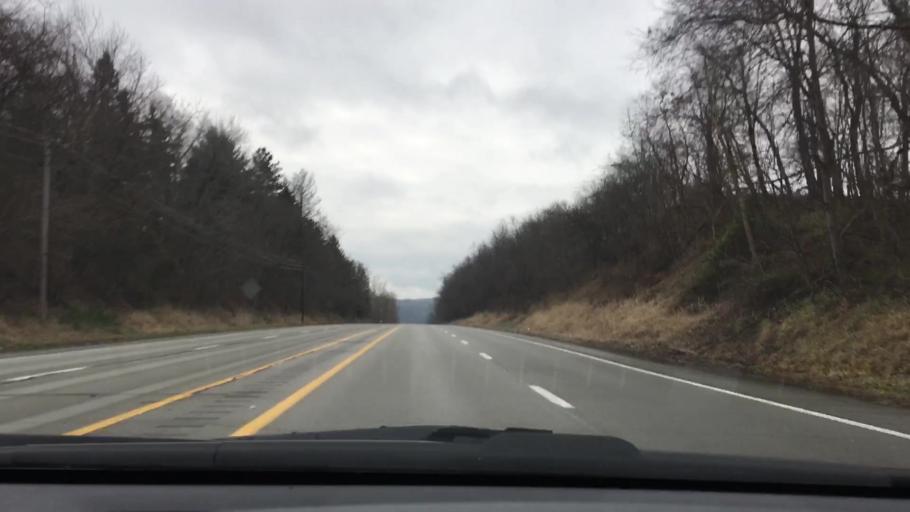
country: US
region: Pennsylvania
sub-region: Fayette County
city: Perryopolis
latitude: 40.1064
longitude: -79.7698
